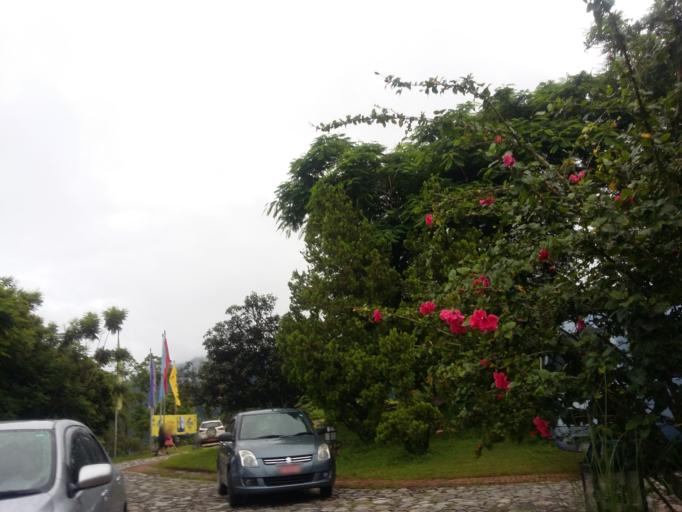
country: NP
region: Western Region
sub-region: Gandaki Zone
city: Pokhara
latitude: 28.1772
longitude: 84.0005
